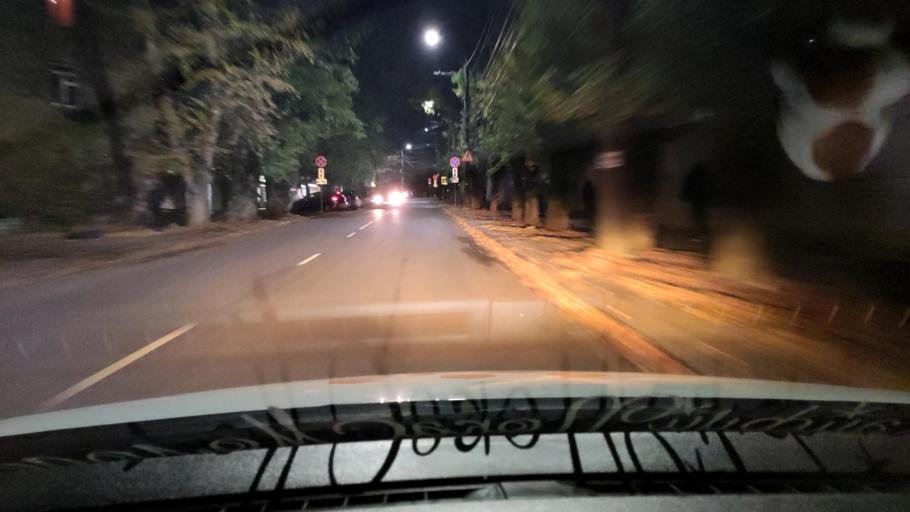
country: RU
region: Voronezj
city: Voronezh
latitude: 51.6852
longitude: 39.1786
